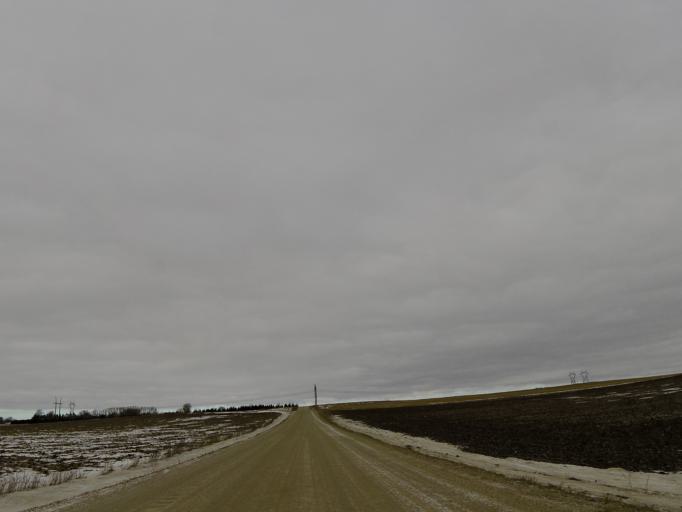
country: US
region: Minnesota
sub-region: Dakota County
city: Hastings
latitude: 44.8099
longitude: -92.8415
